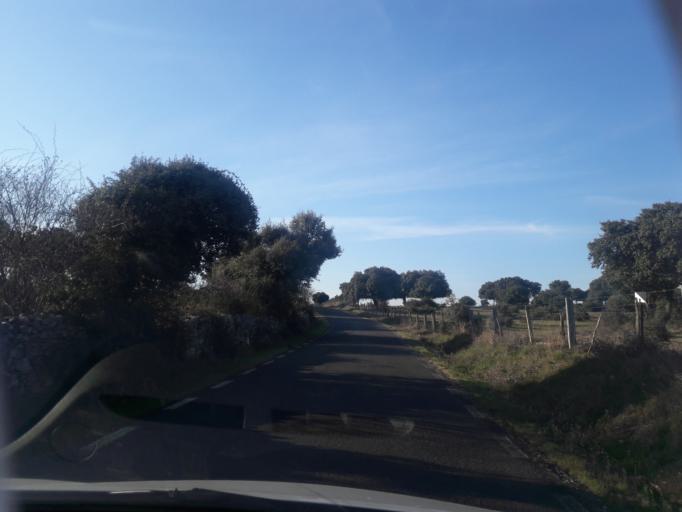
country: ES
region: Castille and Leon
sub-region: Provincia de Salamanca
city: Montejo
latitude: 40.6195
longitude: -5.6082
